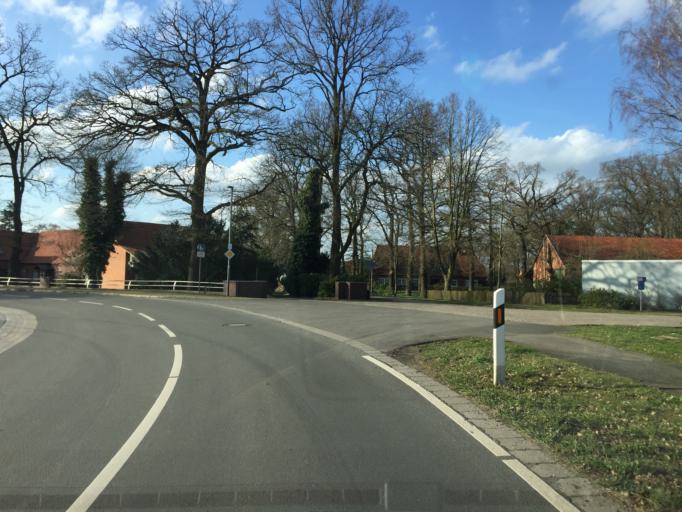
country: DE
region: Lower Saxony
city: Varrel
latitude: 52.6543
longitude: 8.7493
